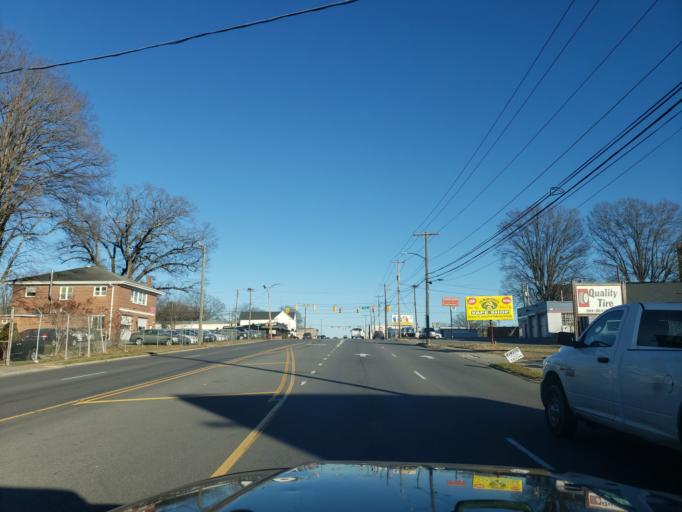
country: US
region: North Carolina
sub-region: Gaston County
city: Gastonia
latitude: 35.2605
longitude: -81.2096
